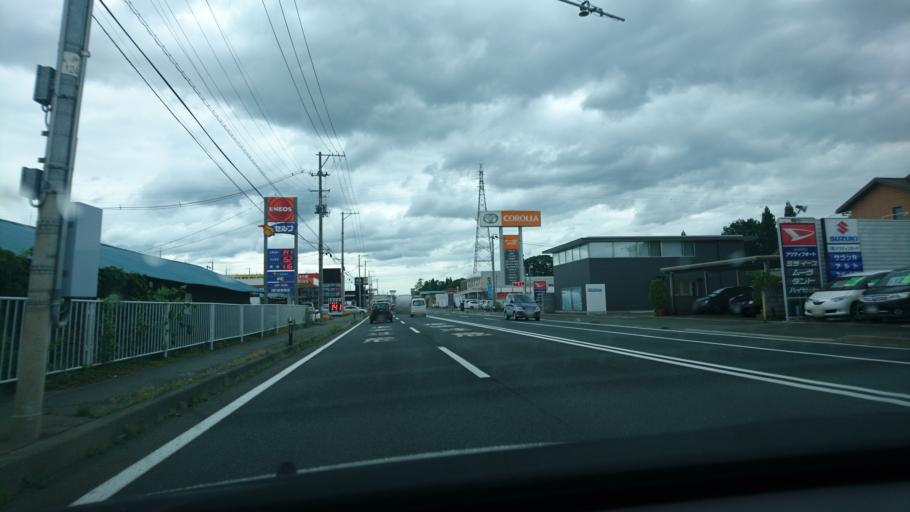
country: JP
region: Iwate
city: Morioka-shi
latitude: 39.7339
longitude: 141.1243
